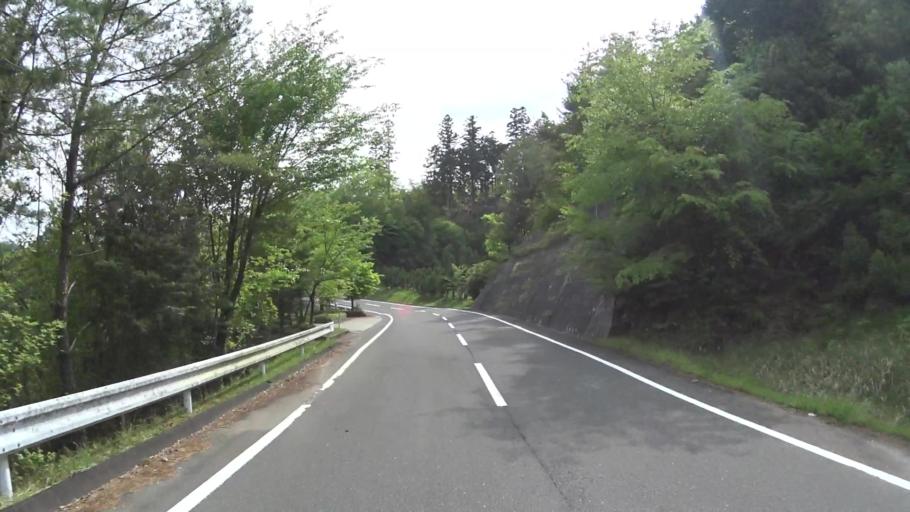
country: JP
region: Kyoto
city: Kameoka
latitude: 35.1497
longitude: 135.6254
